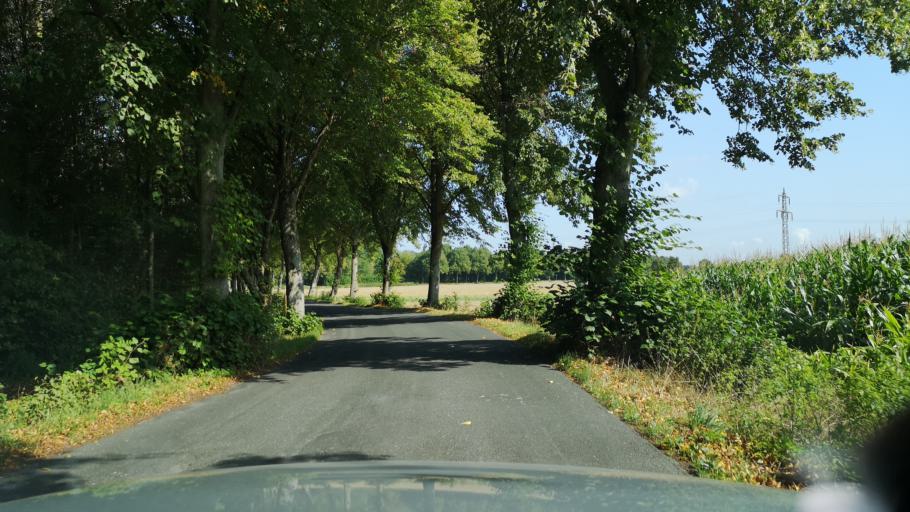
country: DE
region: North Rhine-Westphalia
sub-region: Regierungsbezirk Arnsberg
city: Frondenberg
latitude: 51.4913
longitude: 7.7659
